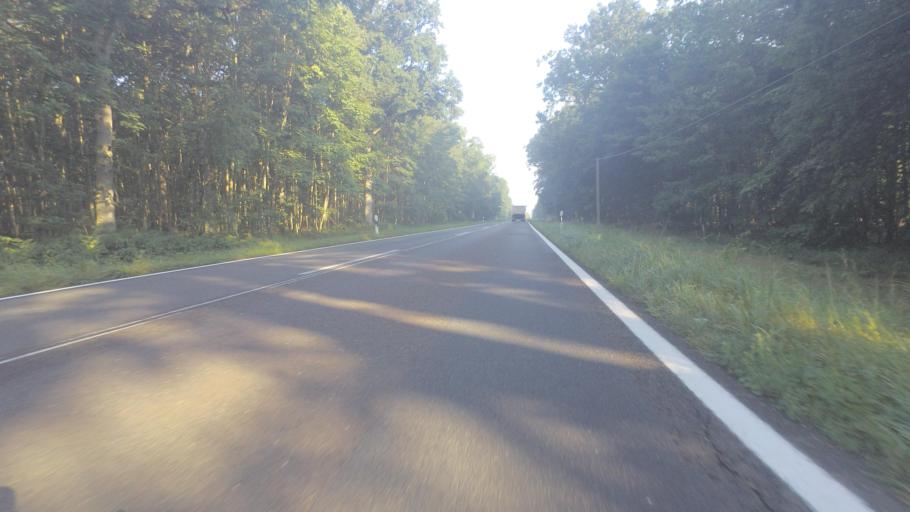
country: DE
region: Mecklenburg-Vorpommern
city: Grimmen
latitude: 54.0380
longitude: 13.1263
